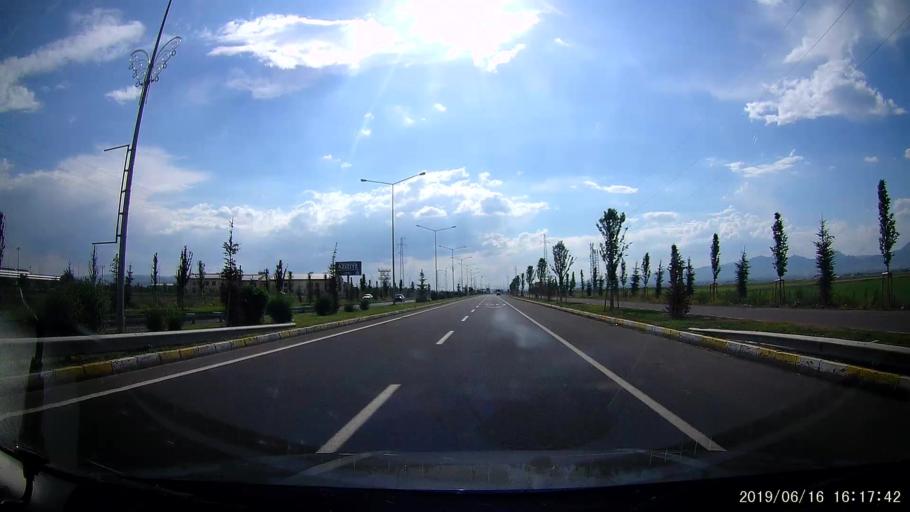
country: TR
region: Erzurum
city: Ilica
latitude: 39.9642
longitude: 41.1817
